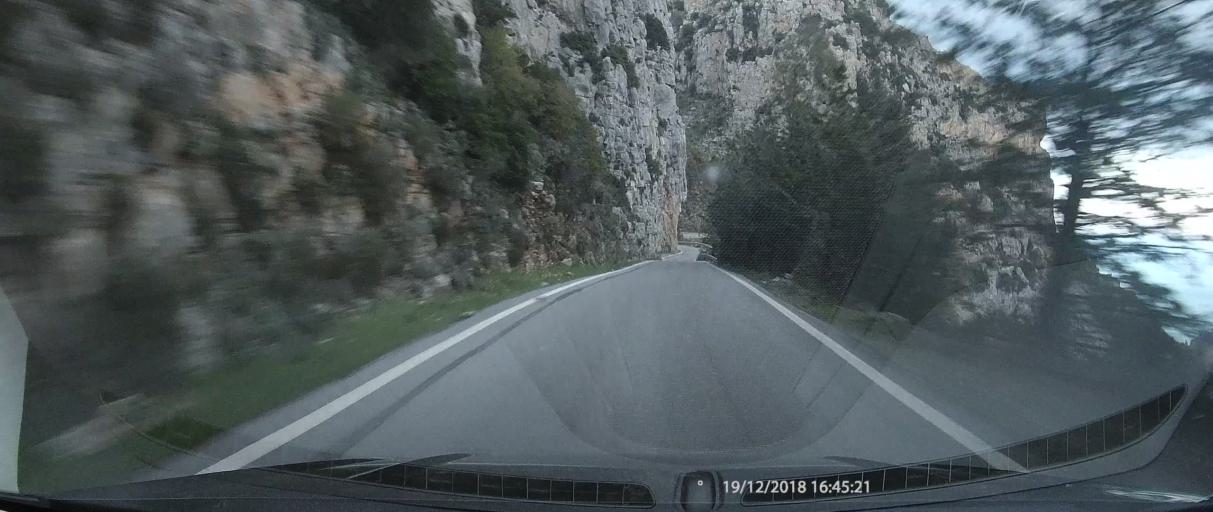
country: GR
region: Peloponnese
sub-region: Nomos Lakonias
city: Sykea
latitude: 36.9180
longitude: 23.0034
